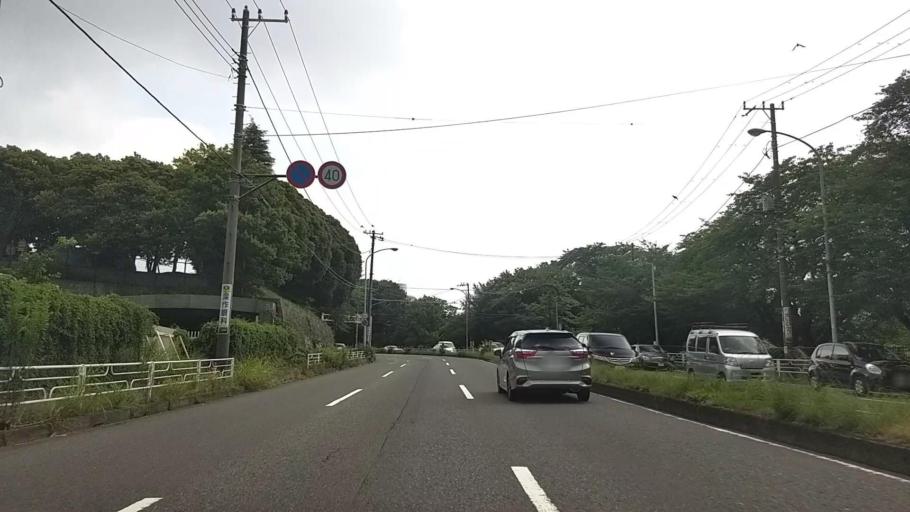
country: JP
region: Kanagawa
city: Yokohama
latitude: 35.4714
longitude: 139.6048
